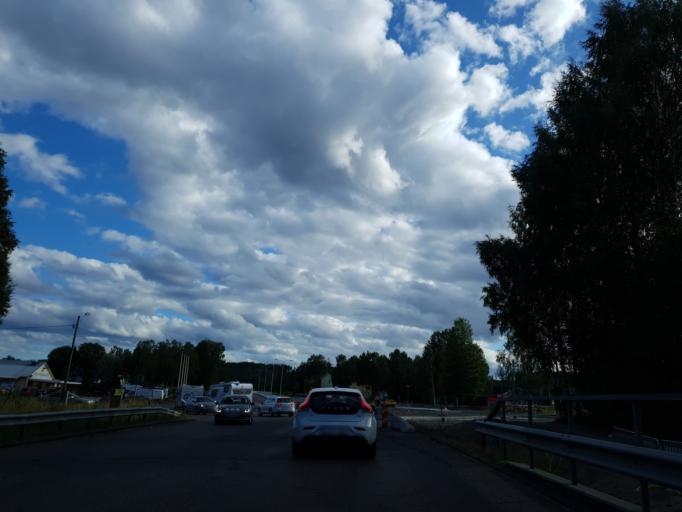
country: SE
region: Vaesternorrland
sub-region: Haernoesands Kommun
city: Haernoesand
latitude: 62.6724
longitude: 17.8397
